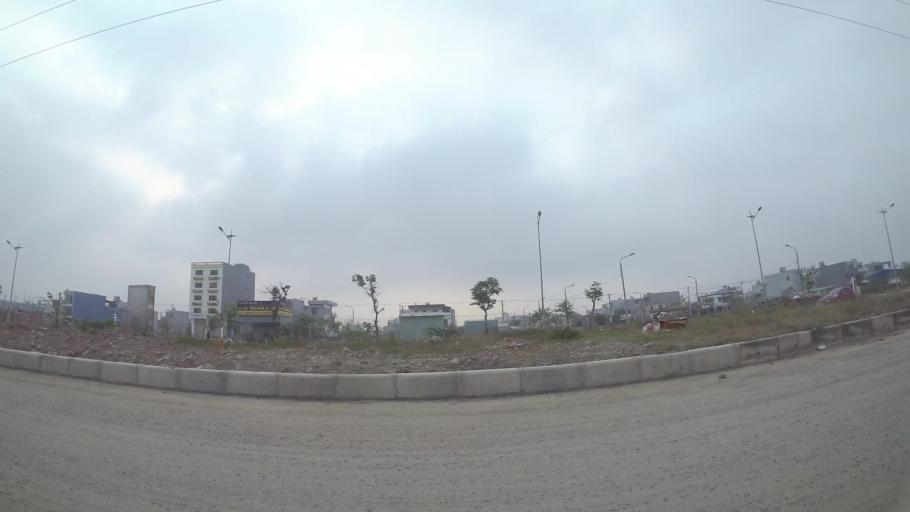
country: VN
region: Da Nang
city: Cam Le
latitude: 16.0127
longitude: 108.2249
